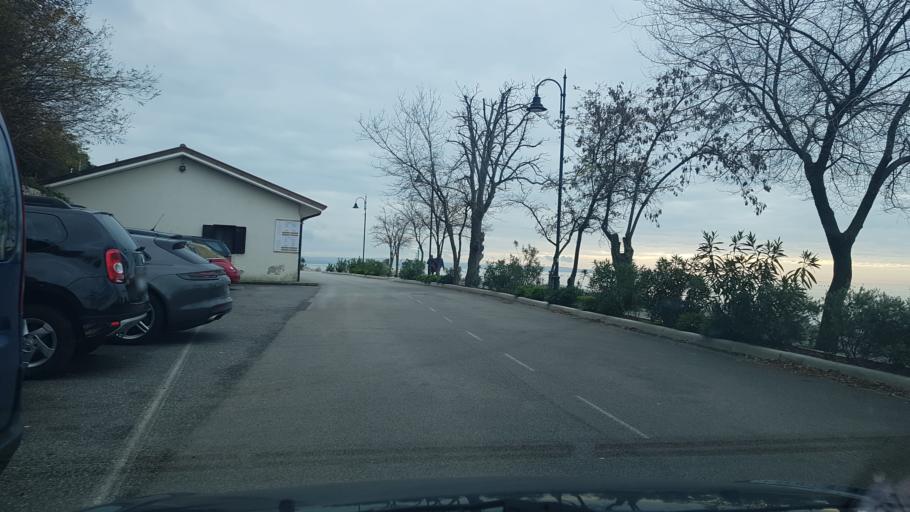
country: IT
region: Friuli Venezia Giulia
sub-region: Provincia di Trieste
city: Sistiana-Visogliano
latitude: 45.7663
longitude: 13.6340
